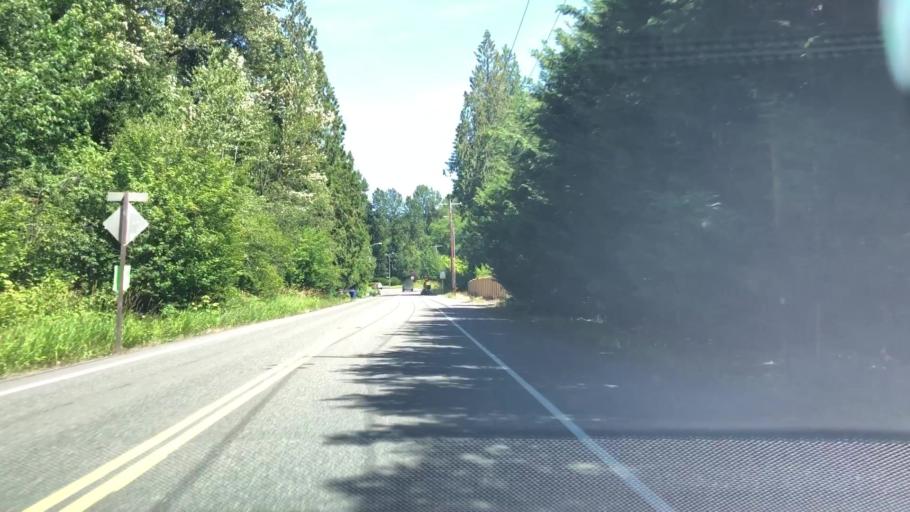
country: US
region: Washington
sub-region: King County
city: Cottage Lake
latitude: 47.7180
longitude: -122.0788
